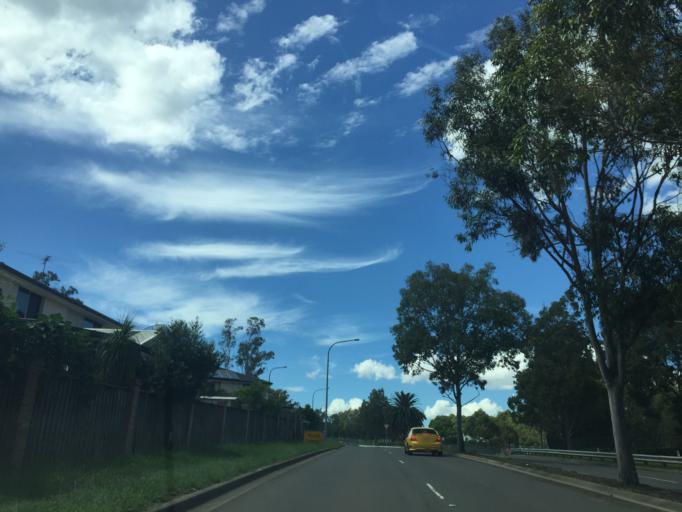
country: AU
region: New South Wales
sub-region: Blacktown
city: Blacktown
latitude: -33.7910
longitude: 150.8935
